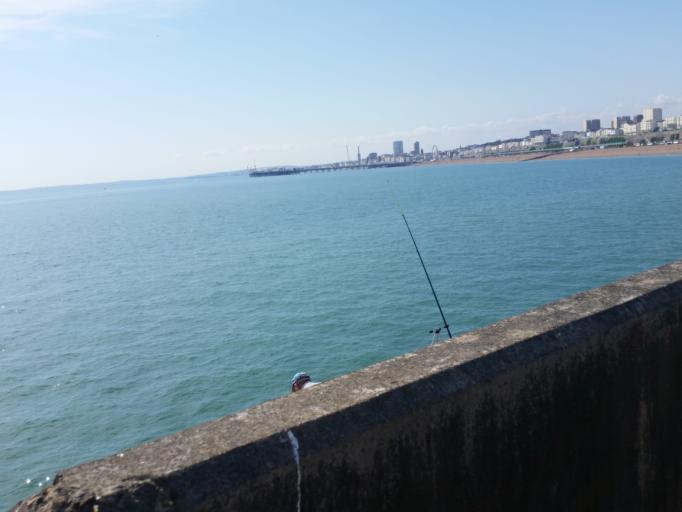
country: GB
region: England
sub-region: Brighton and Hove
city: Brighton
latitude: 50.8097
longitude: -0.1077
